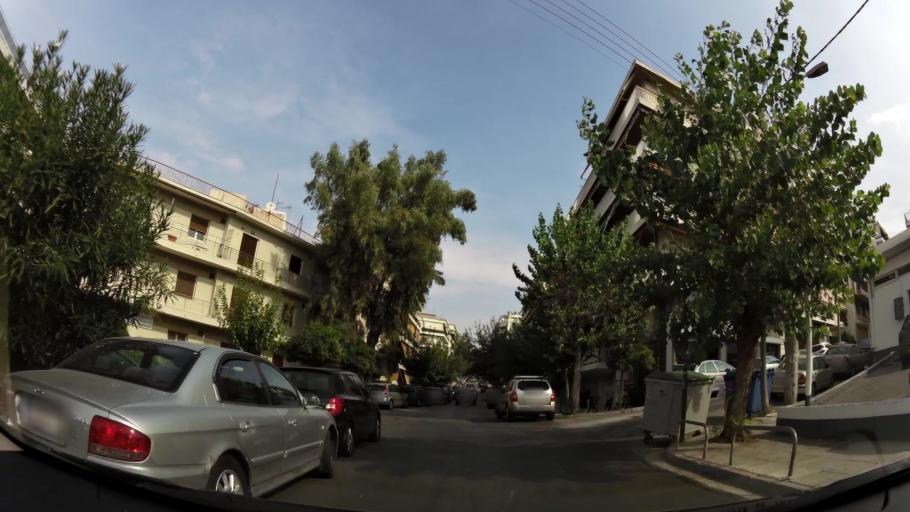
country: GR
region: Attica
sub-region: Nomarchia Athinas
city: Galatsi
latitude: 38.0123
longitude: 23.7552
